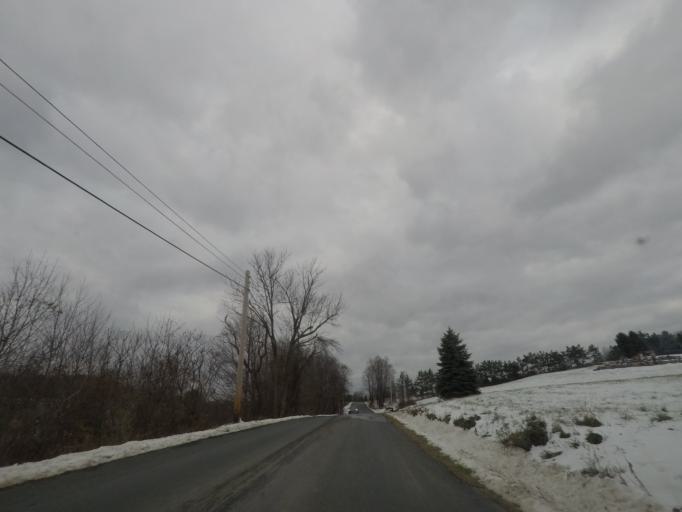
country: US
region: New York
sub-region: Rensselaer County
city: West Sand Lake
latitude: 42.5940
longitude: -73.6307
